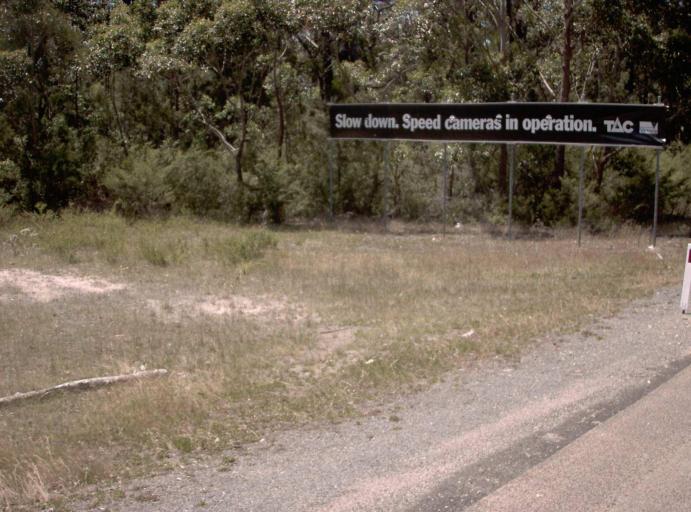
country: AU
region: Victoria
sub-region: East Gippsland
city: Lakes Entrance
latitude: -37.7530
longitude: 148.3320
